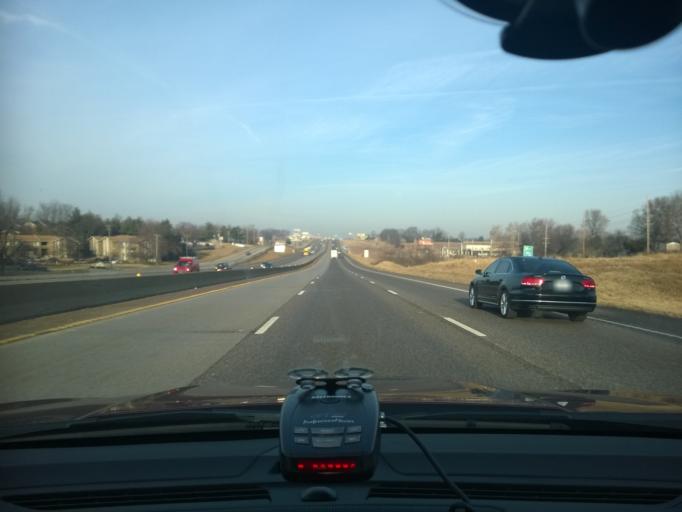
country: US
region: Missouri
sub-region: Saint Charles County
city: Saint Charles
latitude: 38.7890
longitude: -90.5448
